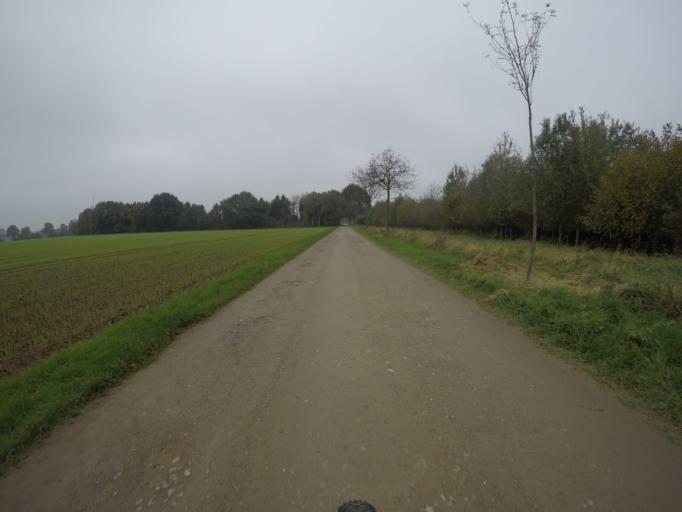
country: DE
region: North Rhine-Westphalia
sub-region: Regierungsbezirk Munster
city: Isselburg
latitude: 51.8272
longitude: 6.5393
